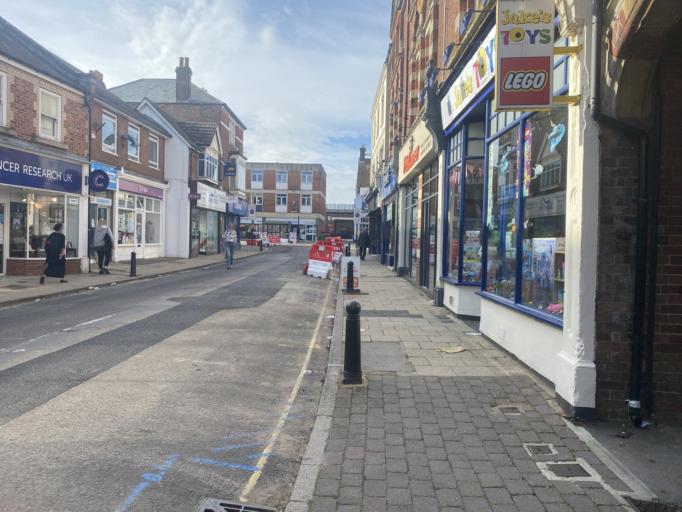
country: GB
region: England
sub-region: Hampshire
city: Petersfield
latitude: 51.0047
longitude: -0.9385
